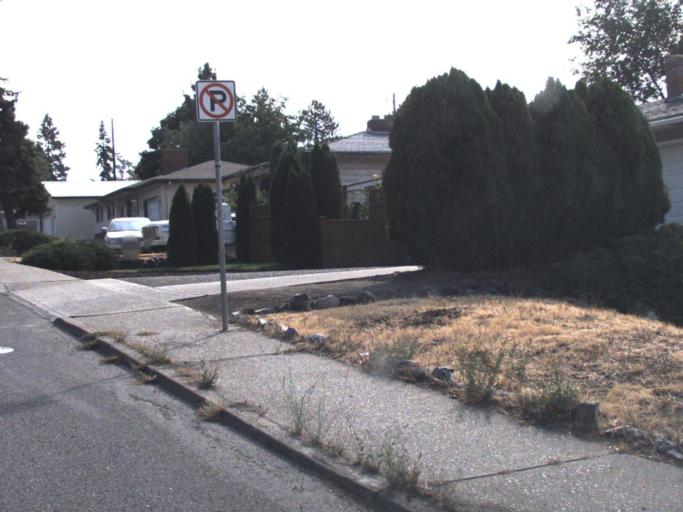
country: US
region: Washington
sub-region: Spokane County
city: Town and Country
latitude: 47.7154
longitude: -117.4706
